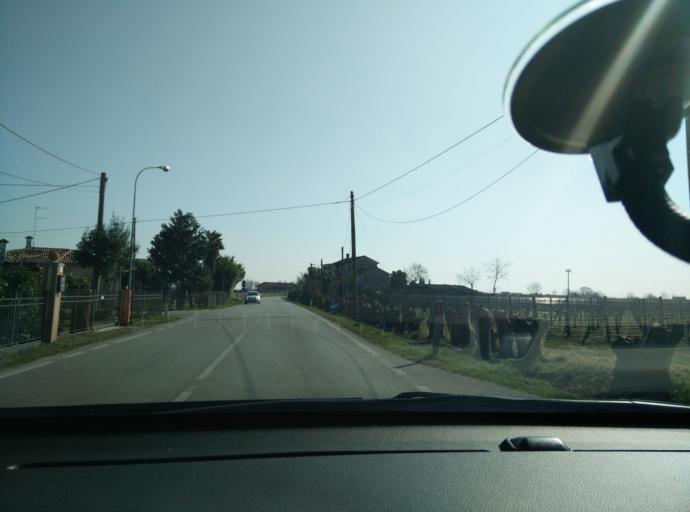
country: IT
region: Veneto
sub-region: Provincia di Treviso
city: Mareno di Piave
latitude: 45.8413
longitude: 12.3201
